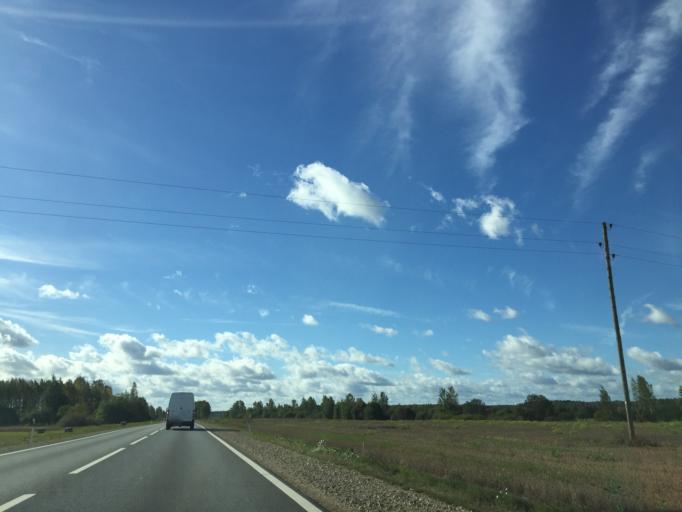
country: LV
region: Plavinu
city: Plavinas
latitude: 56.5929
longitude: 25.7799
